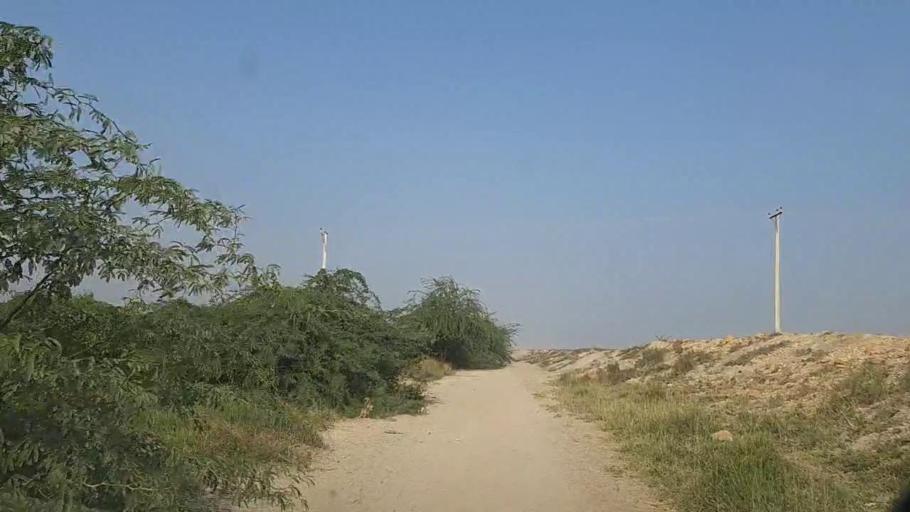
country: PK
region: Sindh
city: Thatta
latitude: 24.6620
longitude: 67.9258
